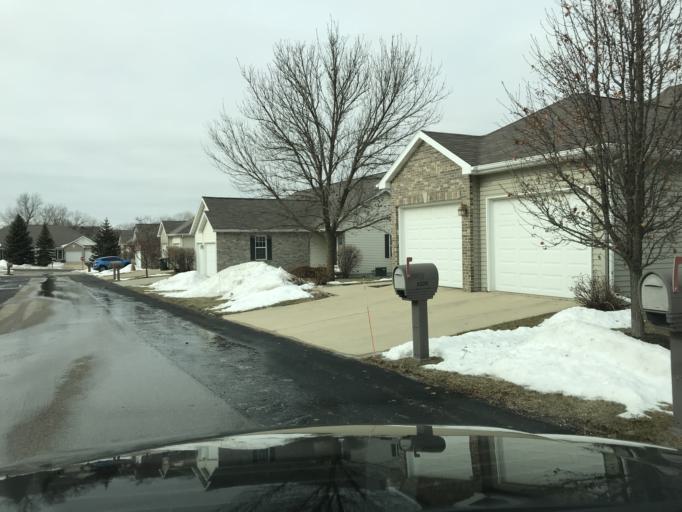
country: US
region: Wisconsin
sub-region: Dane County
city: Monona
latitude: 43.0869
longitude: -89.2698
